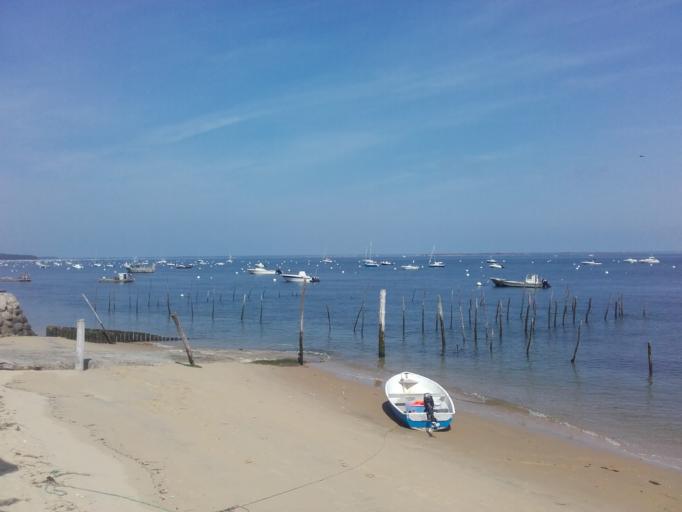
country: FR
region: Aquitaine
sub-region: Departement de la Gironde
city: Arcachon
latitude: 44.6900
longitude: -1.2322
